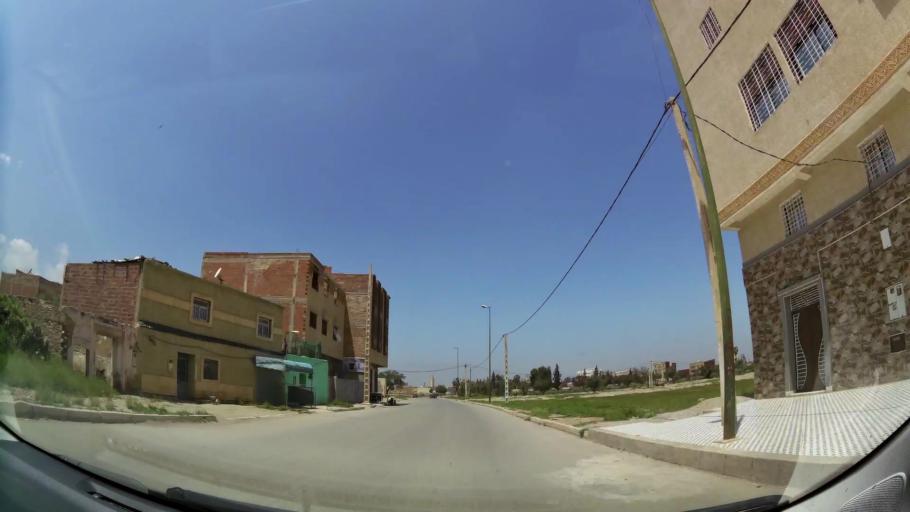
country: MA
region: Oriental
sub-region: Oujda-Angad
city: Oujda
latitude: 34.6889
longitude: -1.8968
